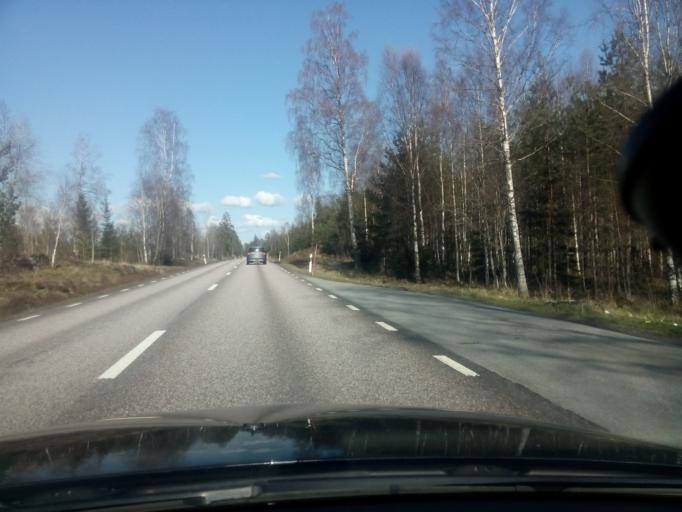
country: SE
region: Soedermanland
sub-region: Flens Kommun
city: Malmkoping
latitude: 59.2063
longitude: 16.8360
